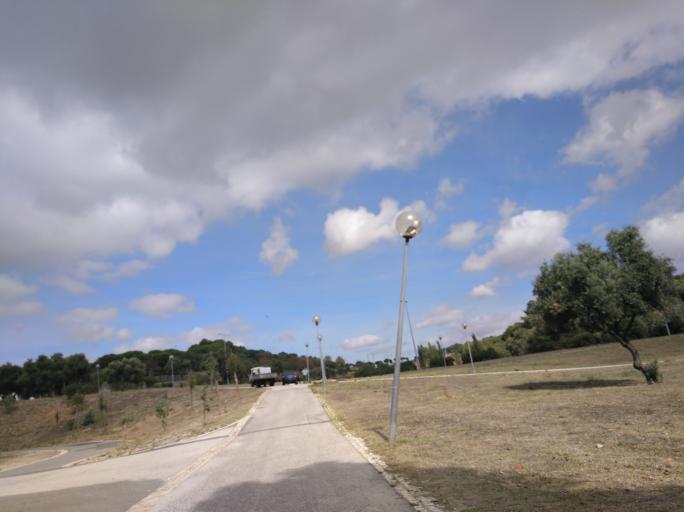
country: PT
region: Lisbon
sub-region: Lisbon
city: Lisbon
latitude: 38.7460
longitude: -9.1249
